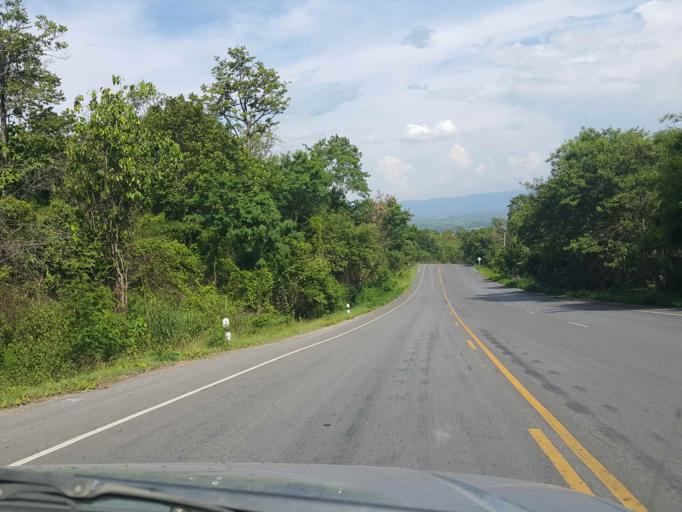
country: TH
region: Lampang
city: Wang Nuea
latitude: 19.1601
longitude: 99.5859
